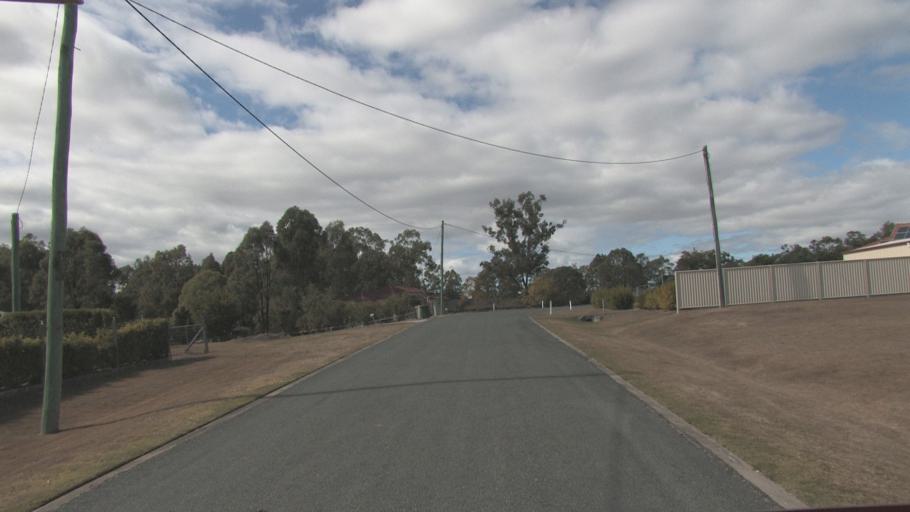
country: AU
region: Queensland
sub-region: Logan
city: Cedar Vale
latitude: -27.8759
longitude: 153.0035
